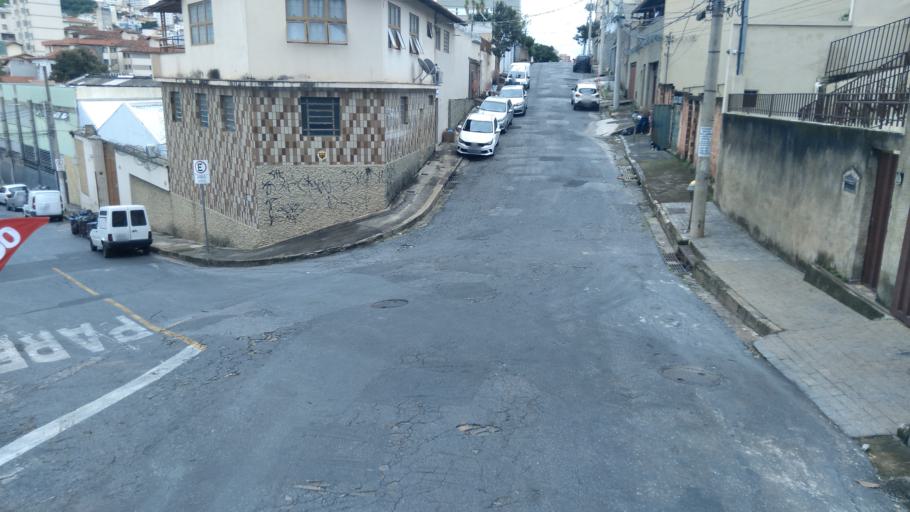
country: BR
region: Minas Gerais
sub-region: Belo Horizonte
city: Belo Horizonte
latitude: -19.9233
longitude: -43.9087
